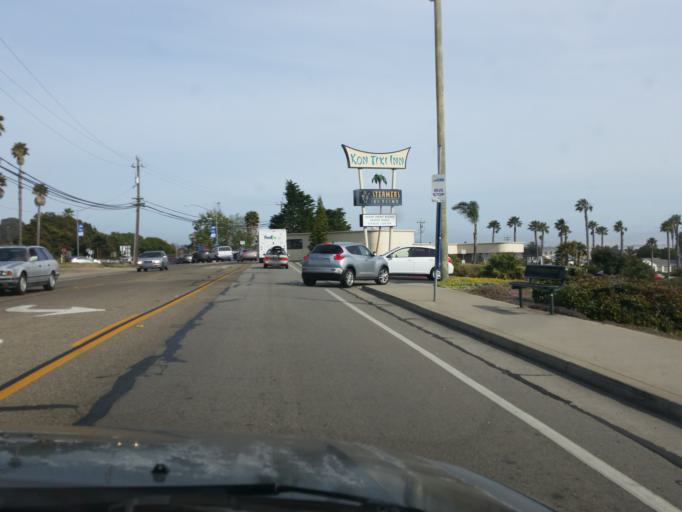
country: US
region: California
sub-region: San Luis Obispo County
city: Pismo Beach
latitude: 35.1471
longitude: -120.6462
